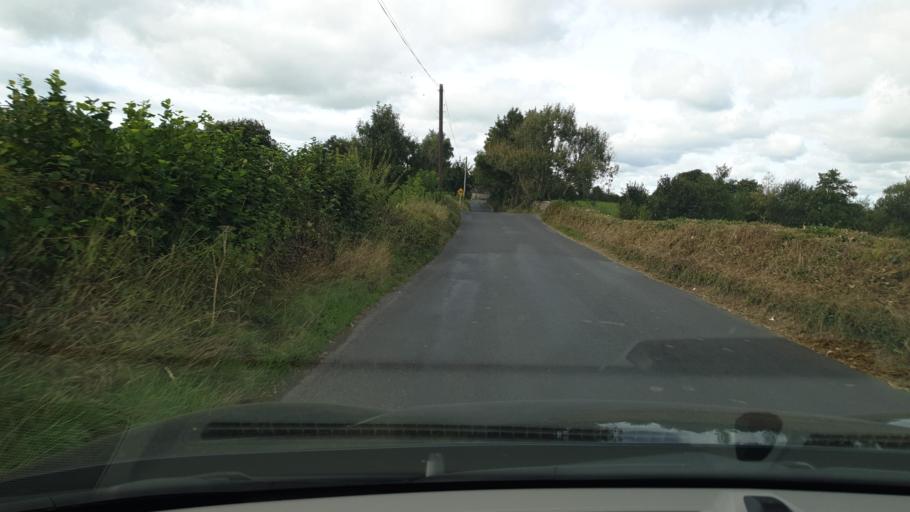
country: IE
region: Leinster
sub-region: Laois
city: Mountmellick
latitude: 53.0864
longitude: -7.2913
